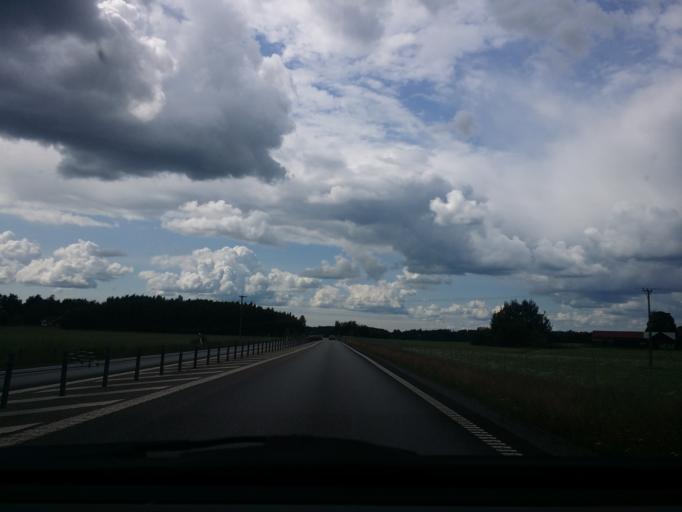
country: SE
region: Vaestmanland
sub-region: Kopings Kommun
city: Koping
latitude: 59.5628
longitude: 16.0670
